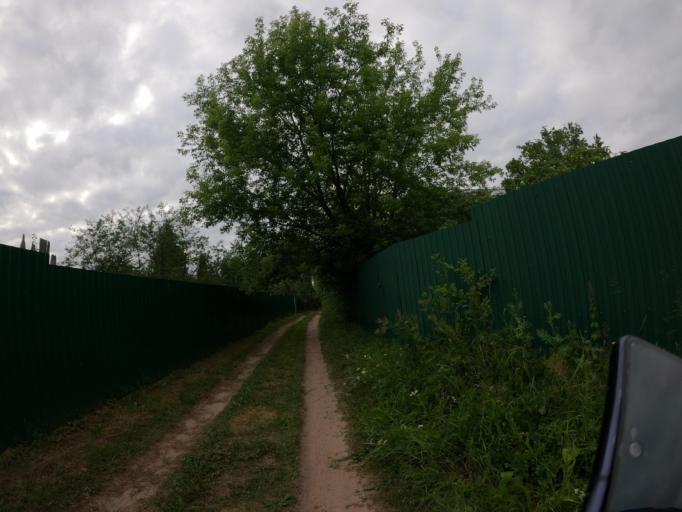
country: RU
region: Moskovskaya
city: Sychevo
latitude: 54.9094
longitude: 38.7326
